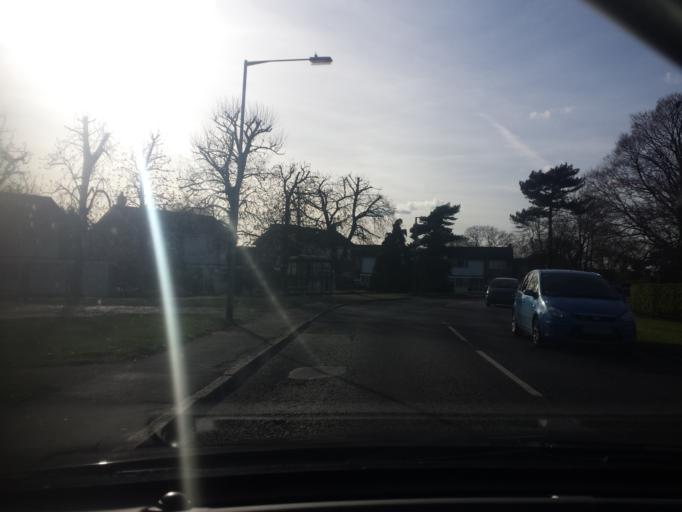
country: GB
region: England
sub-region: Essex
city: Brightlingsea
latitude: 51.8194
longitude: 1.0213
